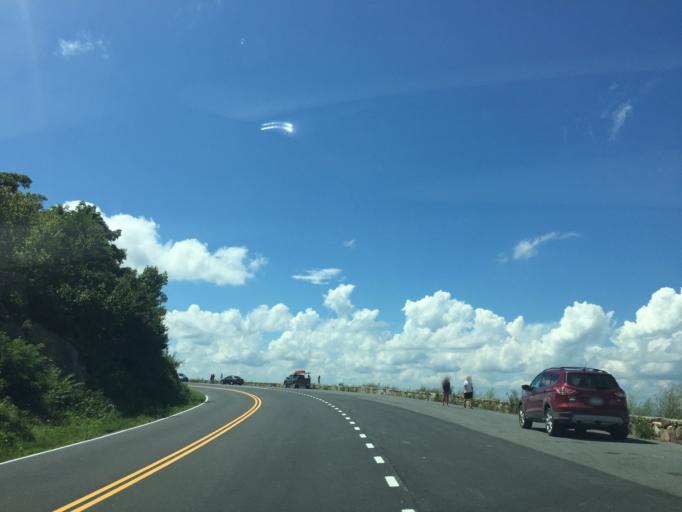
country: US
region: Virginia
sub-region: Rappahannock County
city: Washington
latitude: 38.7626
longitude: -78.2787
